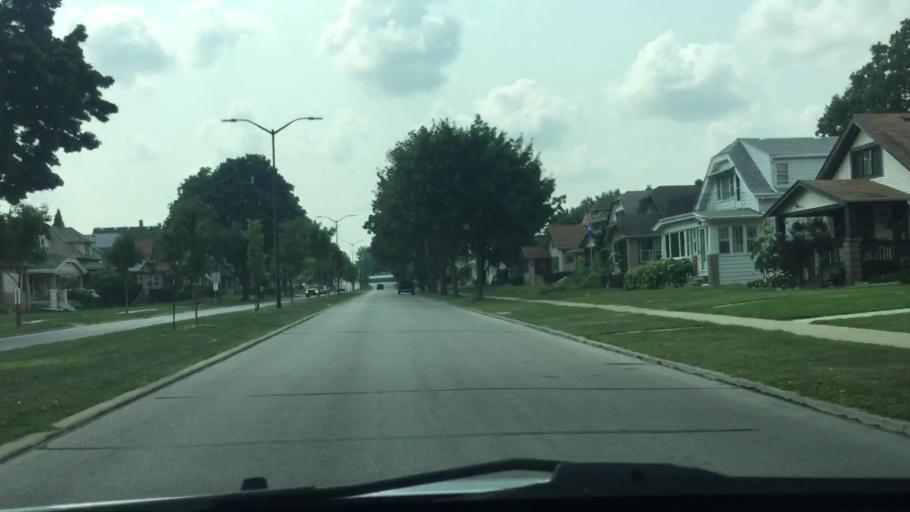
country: US
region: Wisconsin
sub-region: Milwaukee County
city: West Allis
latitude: 43.0201
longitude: -88.0074
